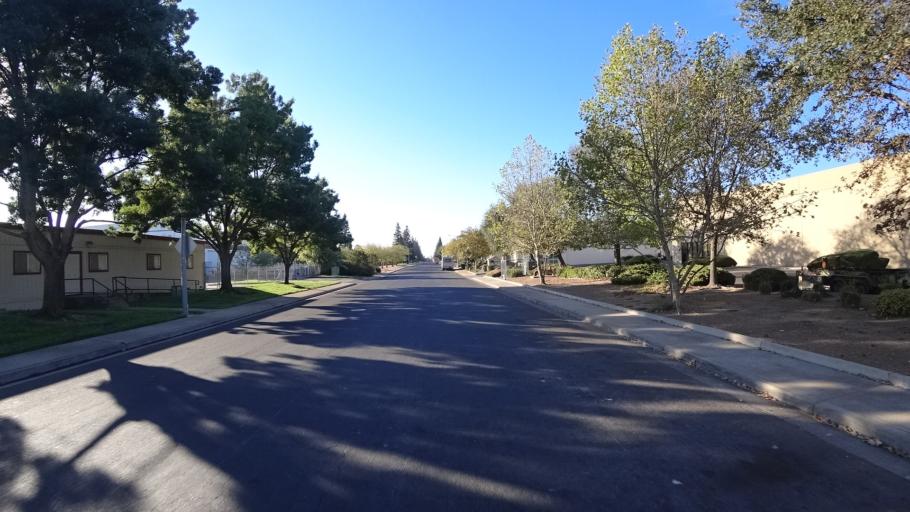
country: US
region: California
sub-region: Sacramento County
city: Florin
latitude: 38.5161
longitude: -121.3848
